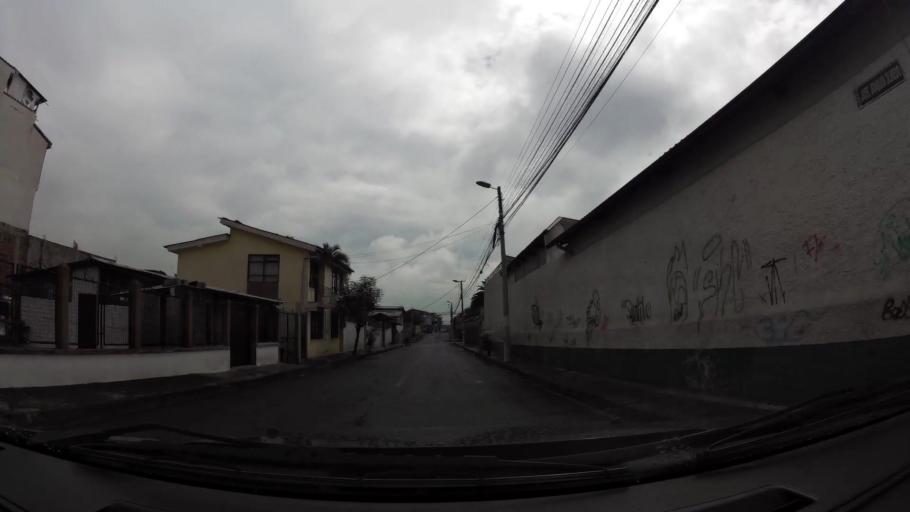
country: EC
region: Pichincha
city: Sangolqui
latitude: -0.2950
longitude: -78.4772
